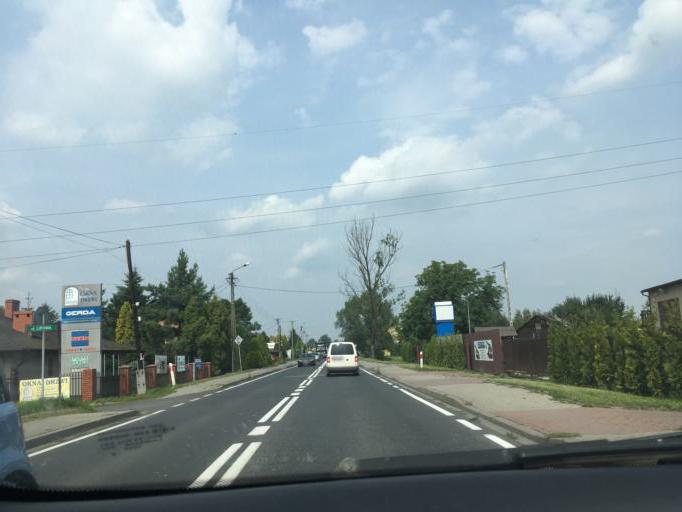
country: PL
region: Lesser Poland Voivodeship
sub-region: Powiat oswiecimski
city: Babice
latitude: 50.0540
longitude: 19.2008
